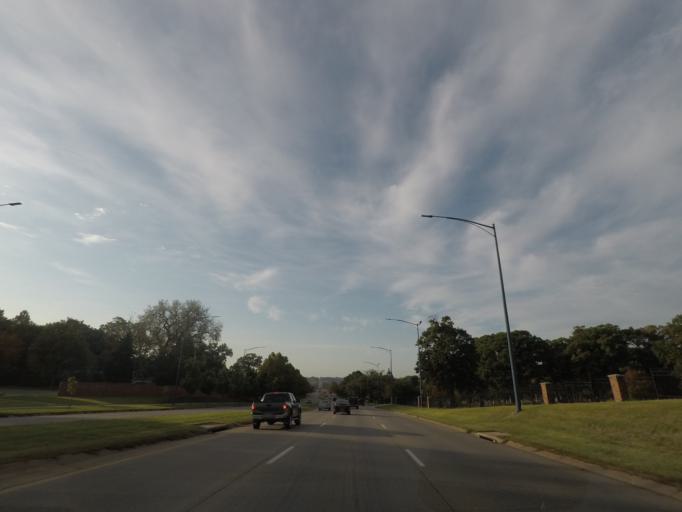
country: US
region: Iowa
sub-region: Polk County
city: Des Moines
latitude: 41.5924
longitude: -93.6447
